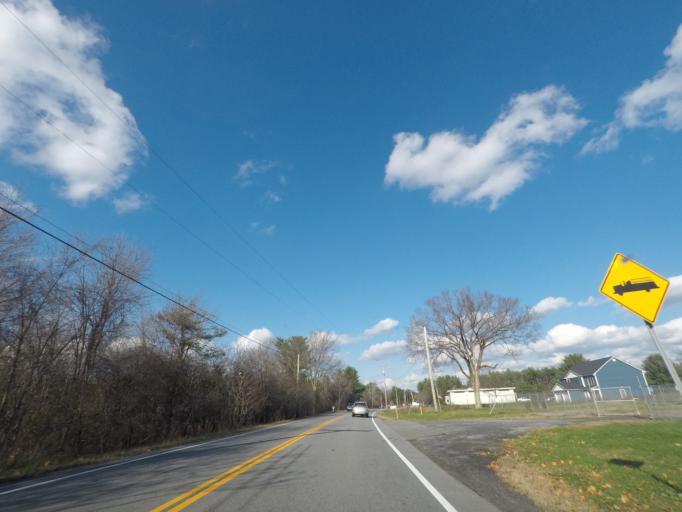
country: US
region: New York
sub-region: Schenectady County
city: East Glenville
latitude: 42.9009
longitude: -73.8757
